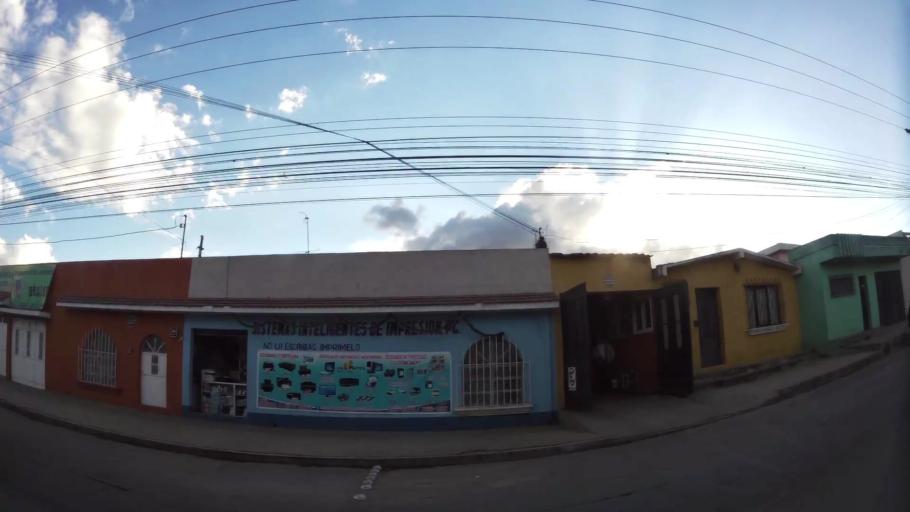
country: GT
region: Quetzaltenango
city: Quetzaltenango
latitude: 14.8532
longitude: -91.5336
